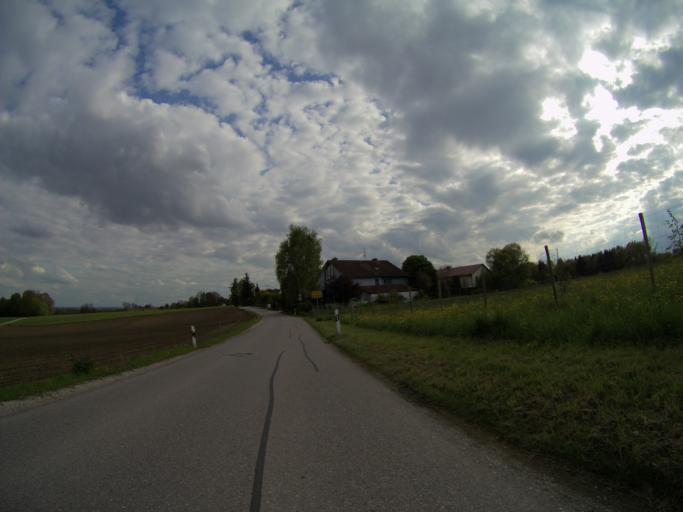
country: DE
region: Bavaria
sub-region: Upper Bavaria
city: Freising
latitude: 48.4138
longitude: 11.7637
